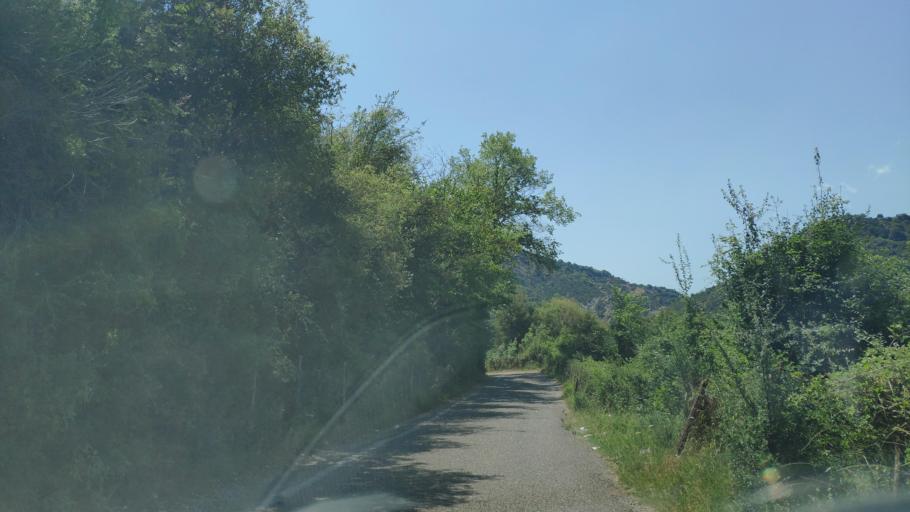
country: GR
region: West Greece
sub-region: Nomos Aitolias kai Akarnanias
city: Krikellos
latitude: 39.0280
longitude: 21.3249
